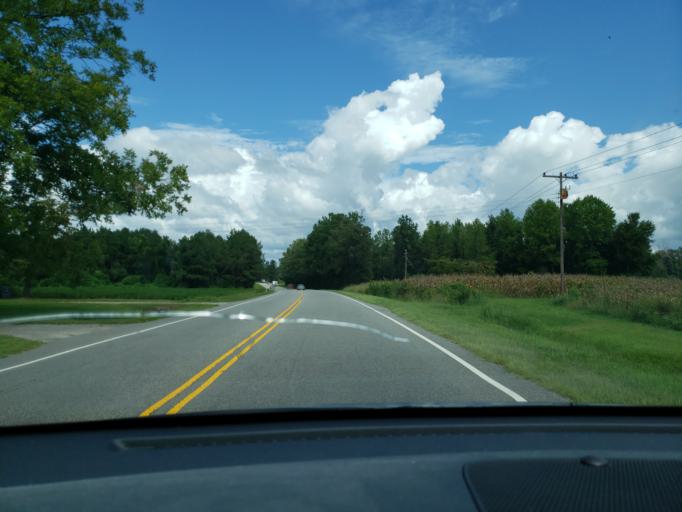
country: US
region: North Carolina
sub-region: Columbus County
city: Brunswick
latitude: 34.2320
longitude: -78.7530
